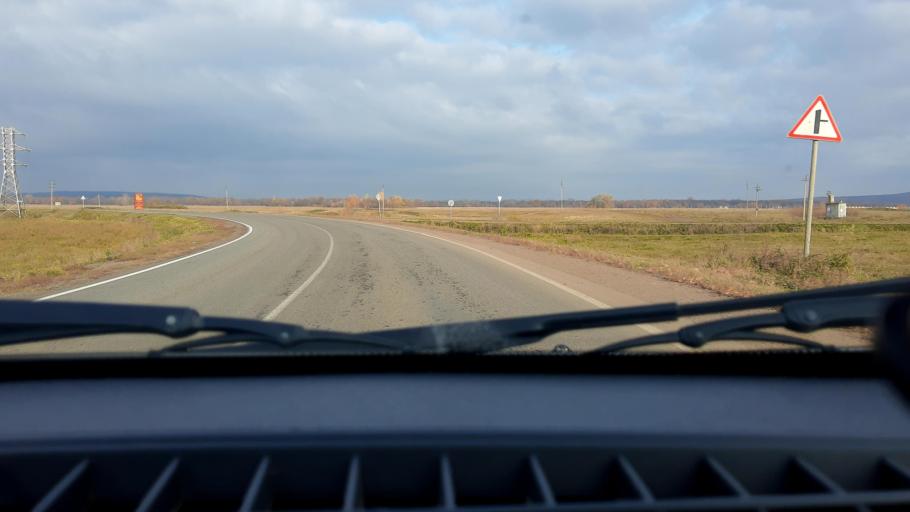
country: RU
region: Bashkortostan
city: Kabakovo
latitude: 54.5531
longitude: 56.0237
